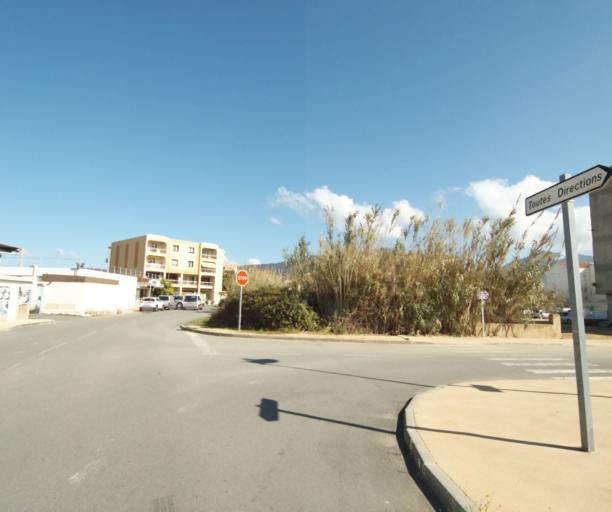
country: FR
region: Corsica
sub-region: Departement de la Corse-du-Sud
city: Propriano
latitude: 41.6741
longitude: 8.8991
